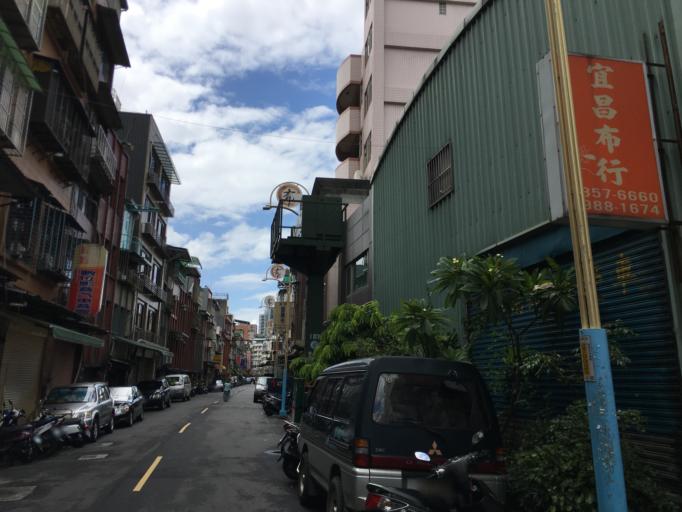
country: TW
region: Taipei
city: Taipei
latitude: 25.0823
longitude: 121.4869
